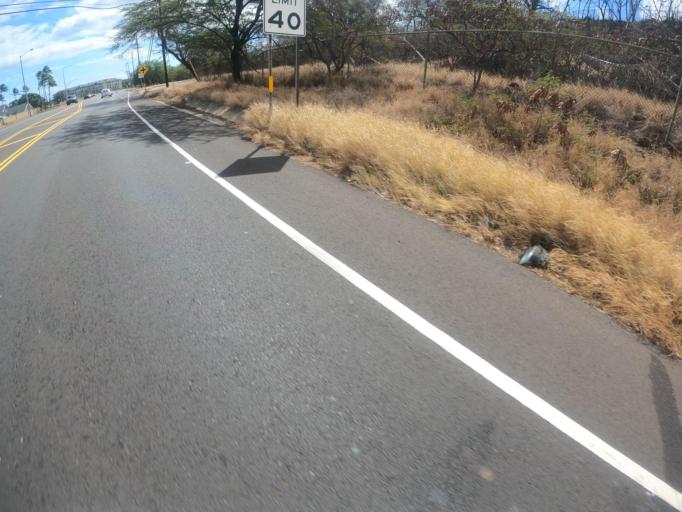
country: US
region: Hawaii
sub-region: Honolulu County
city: Makakilo City
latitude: 21.3353
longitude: -158.0726
